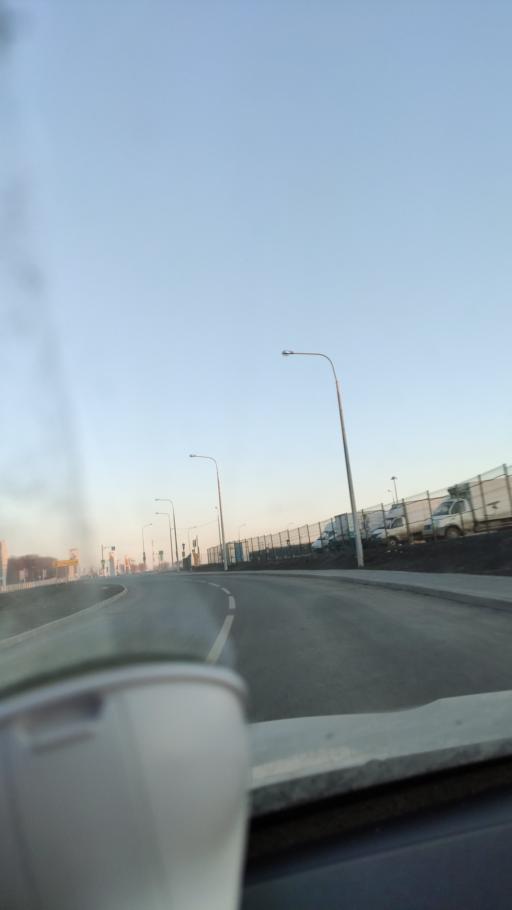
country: RU
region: Samara
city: Petra-Dubrava
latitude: 53.2733
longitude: 50.2549
